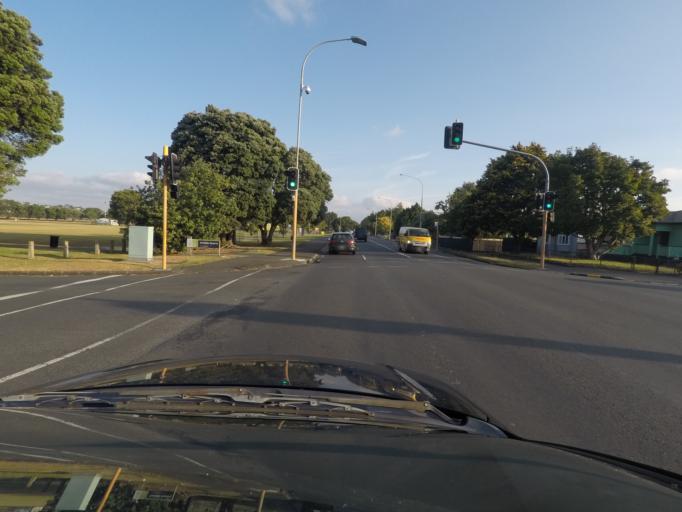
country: NZ
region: Auckland
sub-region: Auckland
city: Rosebank
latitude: -36.8873
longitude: 174.6849
